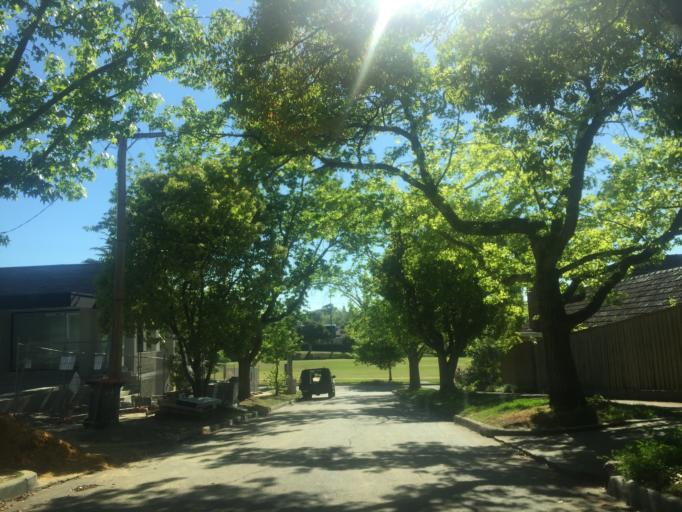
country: AU
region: Victoria
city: Balwyn
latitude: -37.8132
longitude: 145.0693
